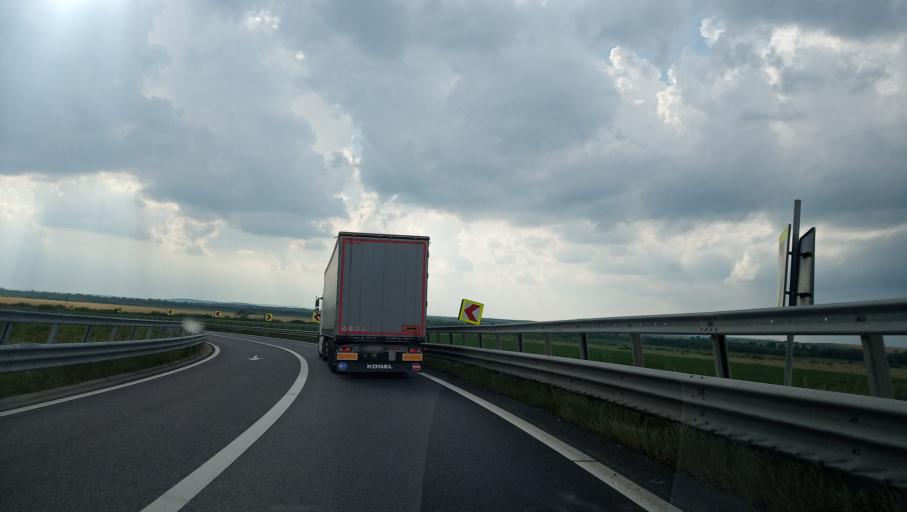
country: RO
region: Timis
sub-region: Comuna Balint
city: Balint
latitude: 45.7986
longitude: 21.8523
